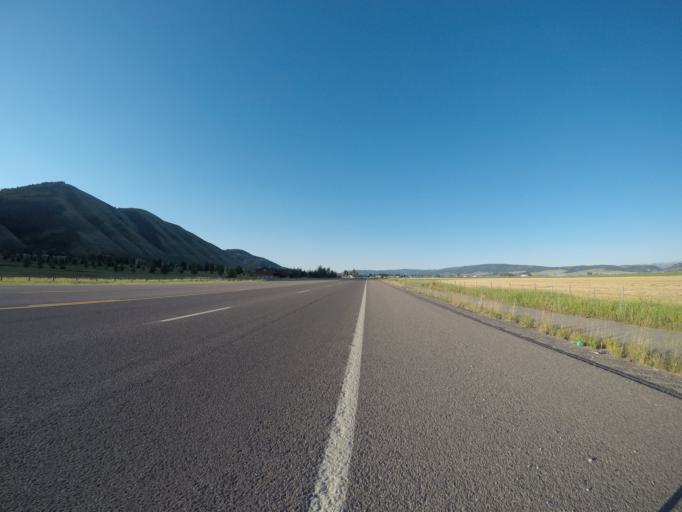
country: US
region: Wyoming
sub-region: Lincoln County
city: Afton
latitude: 42.7060
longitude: -110.9335
